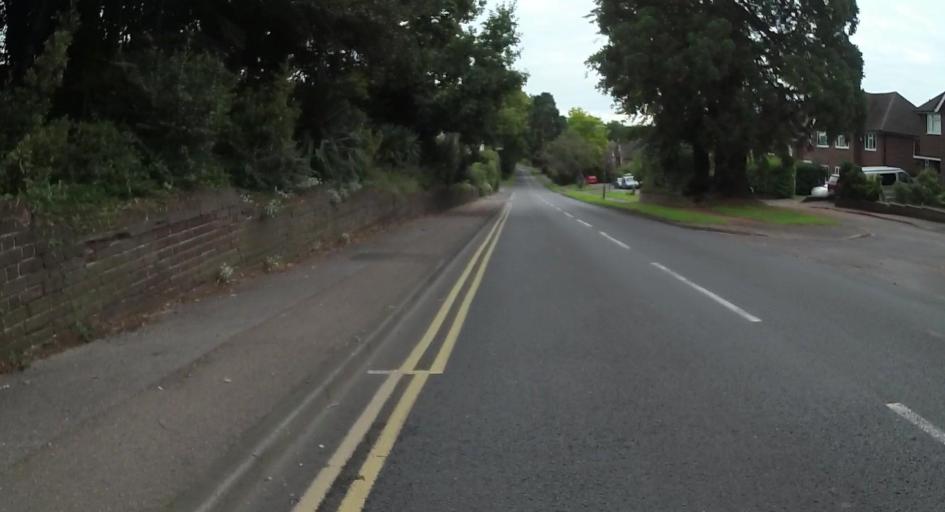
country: GB
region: England
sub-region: Surrey
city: Woking
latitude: 51.3217
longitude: -0.5368
